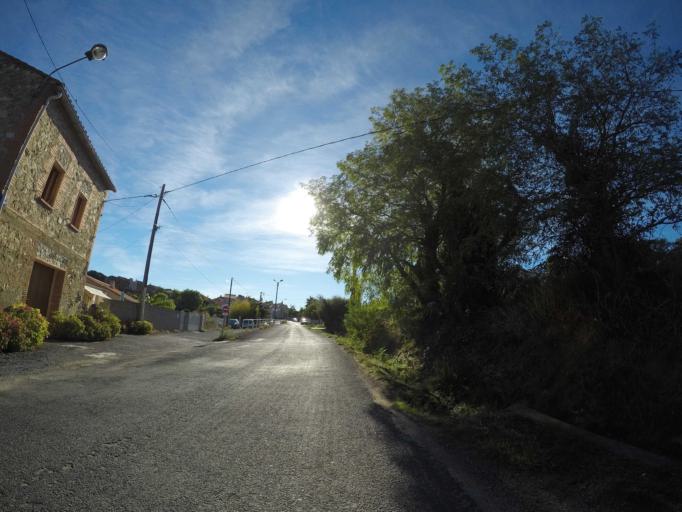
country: FR
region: Languedoc-Roussillon
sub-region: Departement des Pyrenees-Orientales
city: Llupia
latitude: 42.5818
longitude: 2.7755
